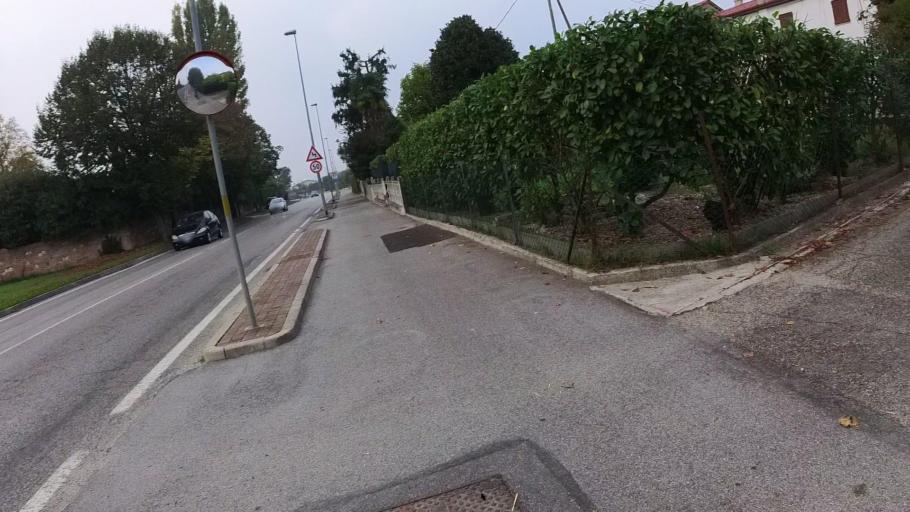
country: IT
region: Veneto
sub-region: Provincia di Venezia
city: Fosso
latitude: 45.3823
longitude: 12.0611
